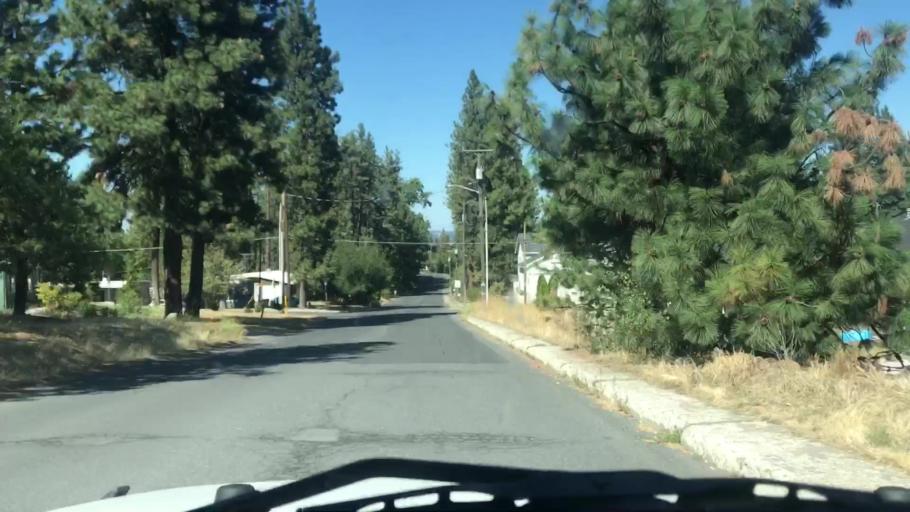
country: US
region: Washington
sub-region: Spokane County
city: Spokane
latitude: 47.6423
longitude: -117.4515
